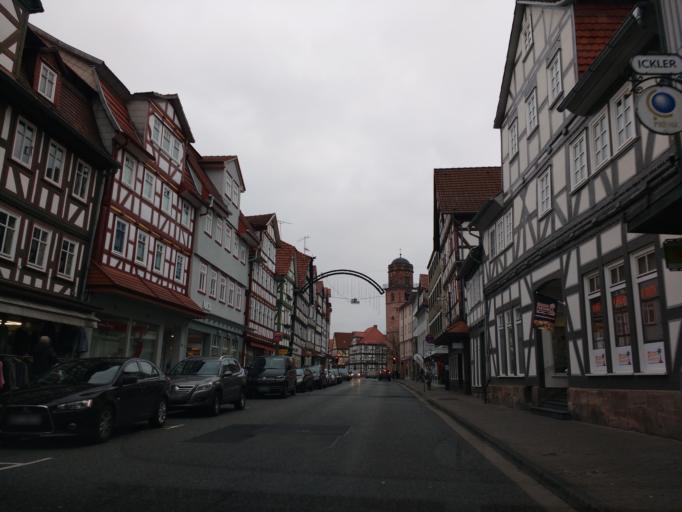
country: DE
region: Hesse
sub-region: Regierungsbezirk Kassel
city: Rotenburg an der Fulda
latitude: 50.9957
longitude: 9.7260
